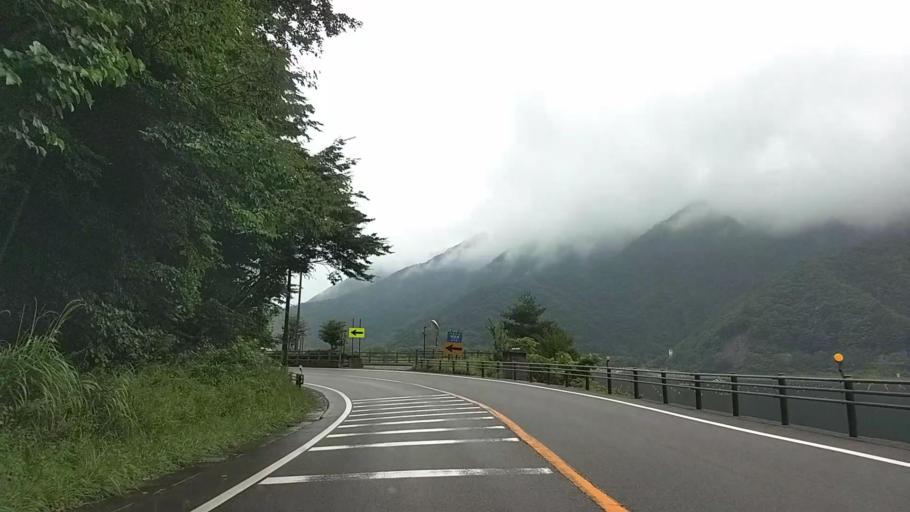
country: JP
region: Yamanashi
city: Fujikawaguchiko
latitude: 35.4924
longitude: 138.6107
